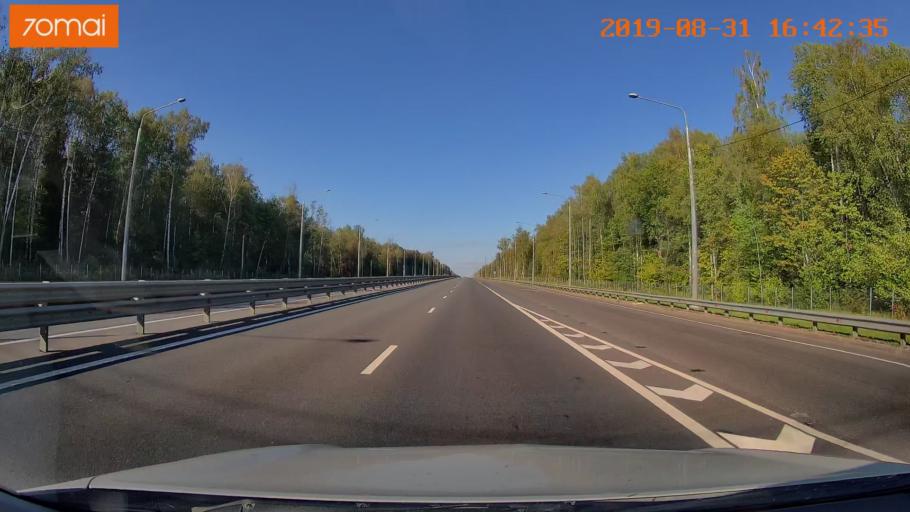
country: RU
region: Kaluga
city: Mstikhino
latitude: 54.5966
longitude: 36.0883
